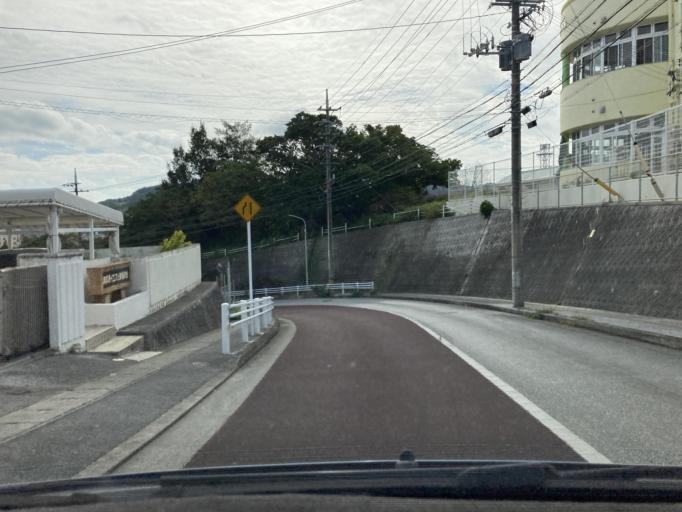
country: JP
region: Okinawa
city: Ginowan
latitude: 26.2034
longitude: 127.7510
